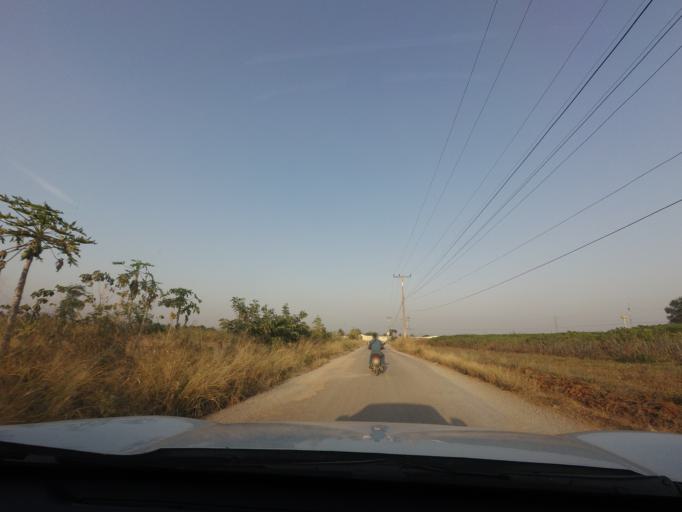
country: TH
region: Nakhon Ratchasima
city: Pak Chong
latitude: 14.6449
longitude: 101.3760
